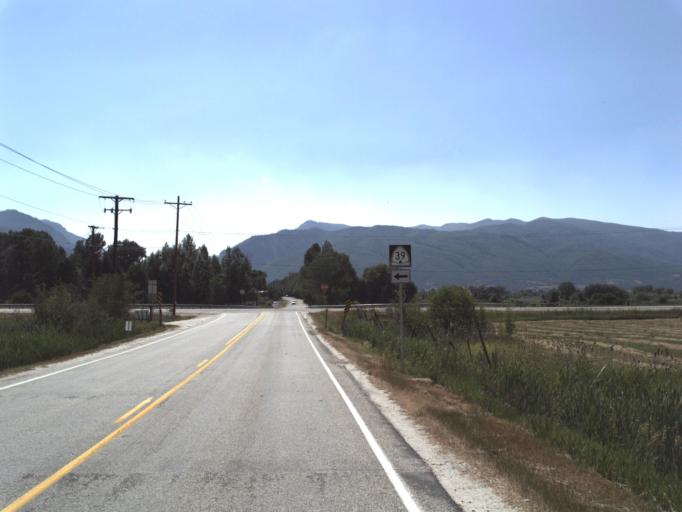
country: US
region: Utah
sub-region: Weber County
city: Wolf Creek
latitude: 41.2623
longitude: -111.7567
